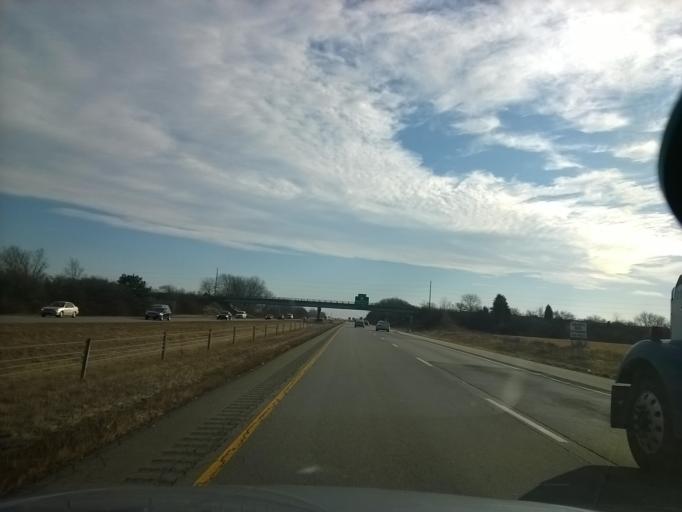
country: US
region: Indiana
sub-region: Johnson County
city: Franklin
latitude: 39.4982
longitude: -86.0182
